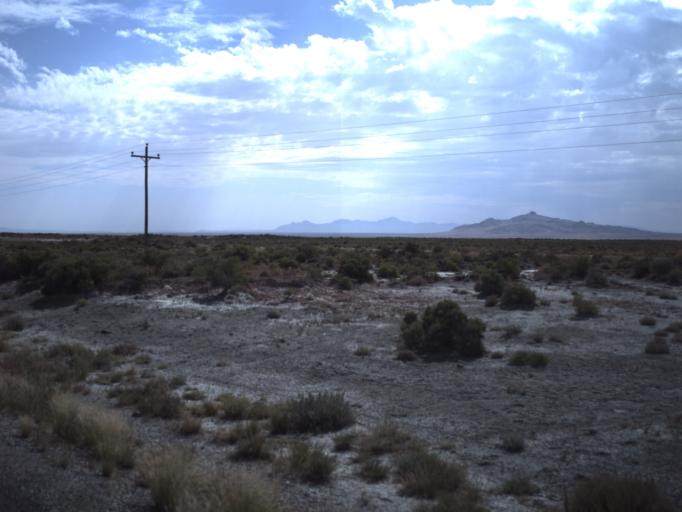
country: US
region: Utah
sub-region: Tooele County
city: Wendover
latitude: 41.4241
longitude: -113.8647
